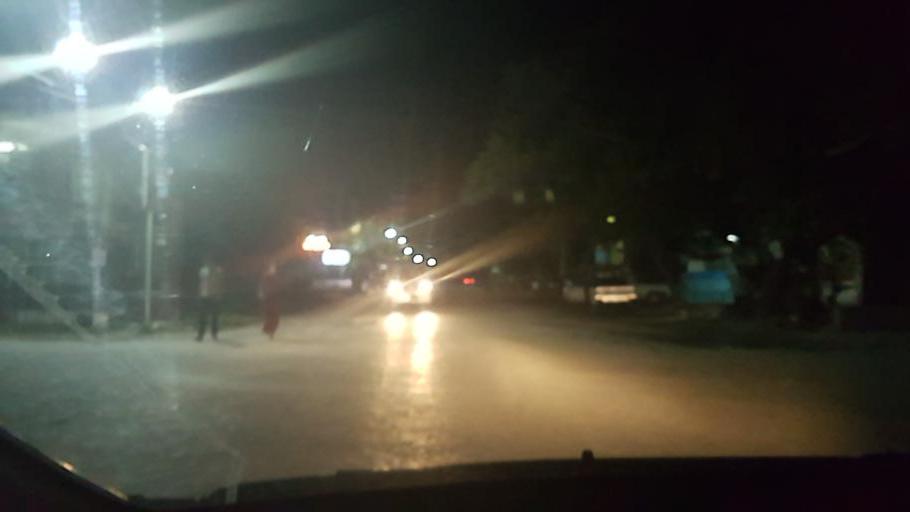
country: MM
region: Mandalay
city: Mandalay
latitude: 21.9810
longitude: 96.0938
